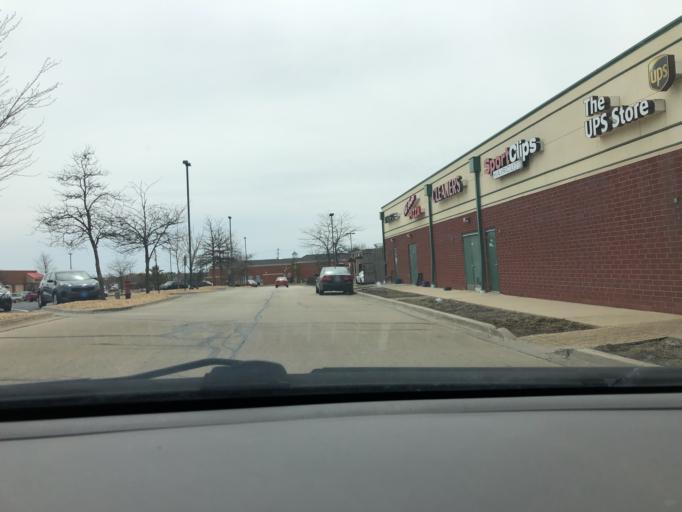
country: US
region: Illinois
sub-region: Kane County
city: South Elgin
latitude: 42.0093
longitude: -88.3353
